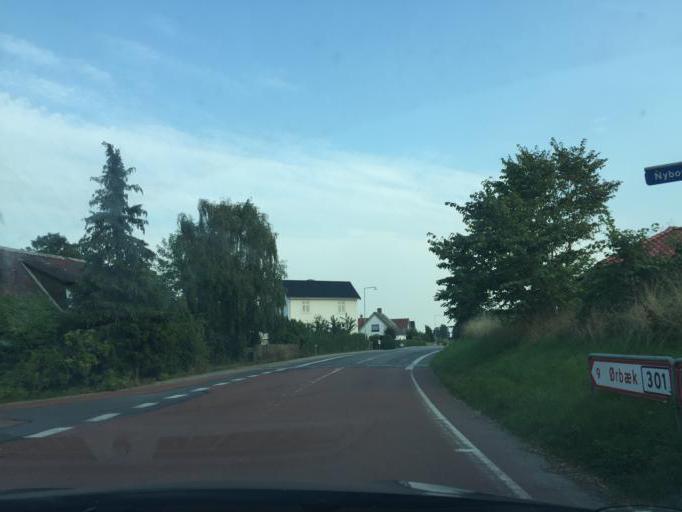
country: DK
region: South Denmark
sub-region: Kerteminde Kommune
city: Langeskov
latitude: 55.3073
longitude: 10.5873
